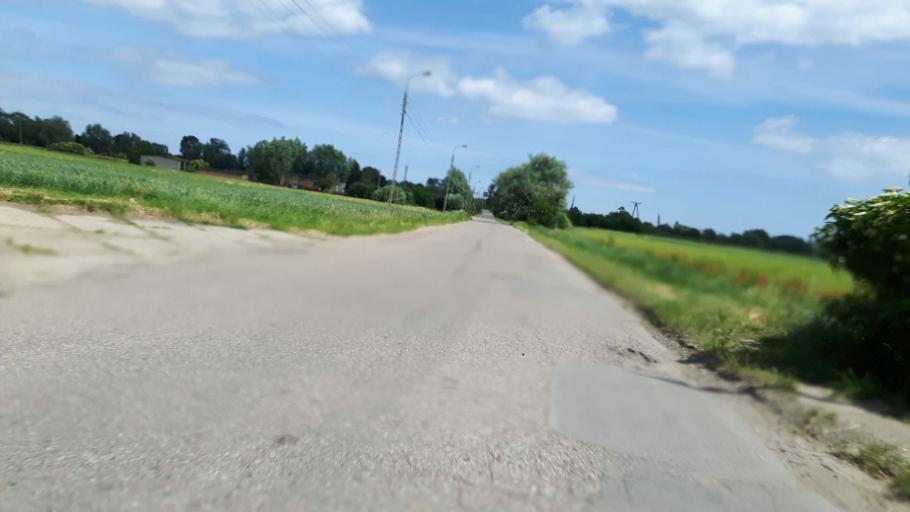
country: PL
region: Pomeranian Voivodeship
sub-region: Powiat gdanski
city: Cedry Wielkie
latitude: 54.3429
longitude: 18.7700
